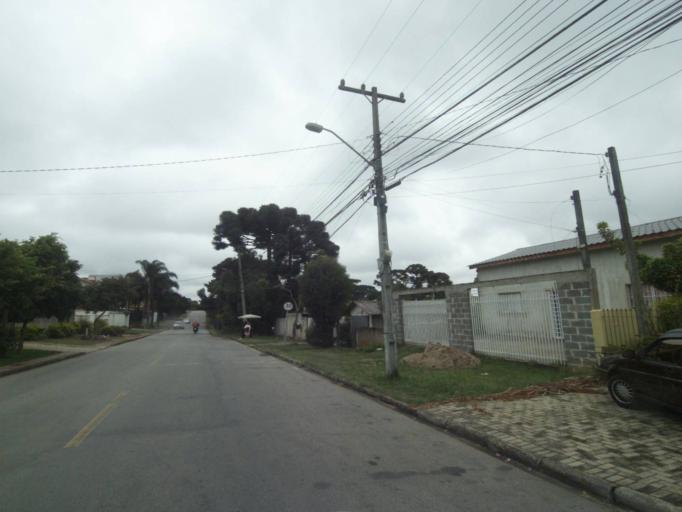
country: BR
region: Parana
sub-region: Curitiba
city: Curitiba
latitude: -25.4215
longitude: -49.3354
